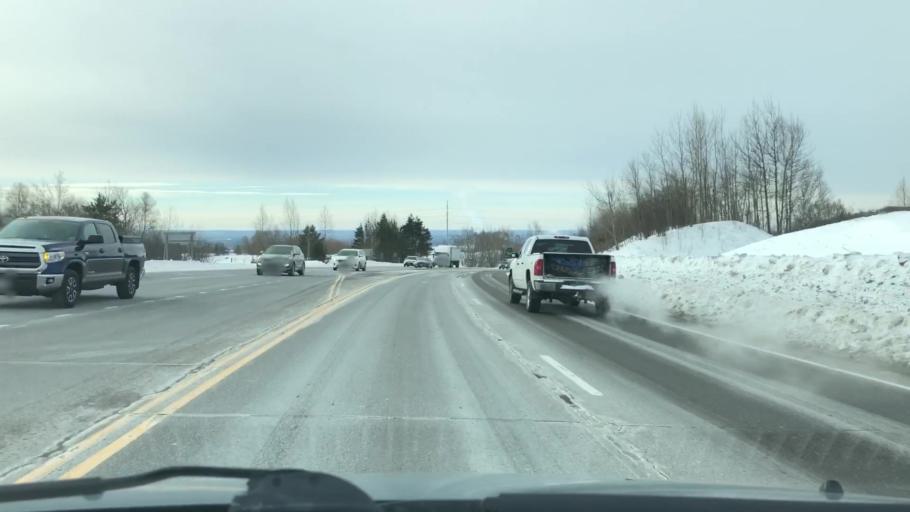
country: US
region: Minnesota
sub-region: Saint Louis County
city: Duluth
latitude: 46.7817
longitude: -92.1388
